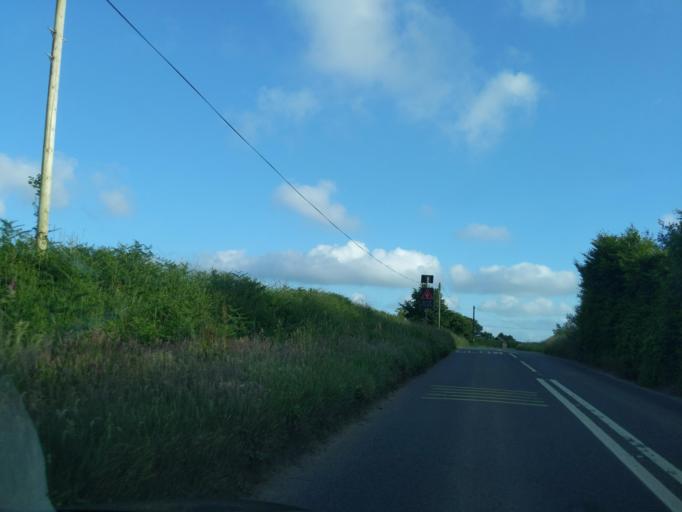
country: GB
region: England
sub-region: Devon
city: Great Torrington
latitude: 50.9805
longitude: -4.0948
